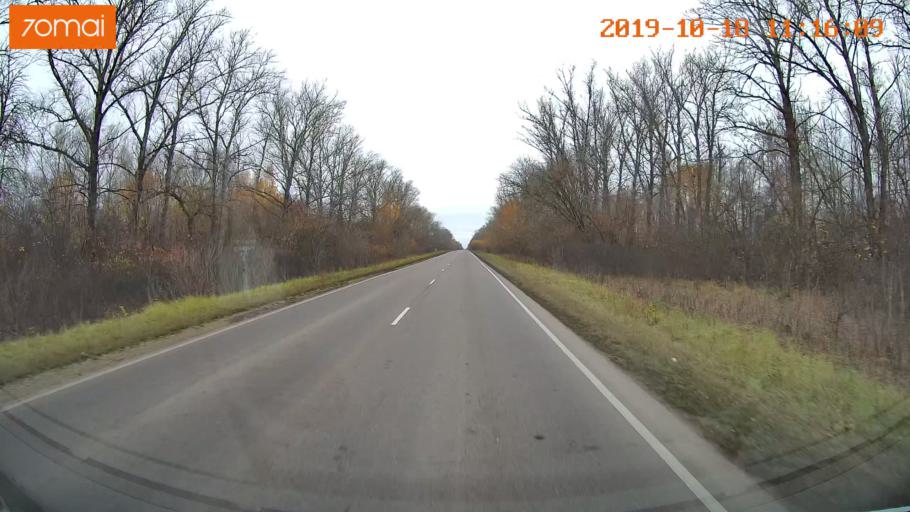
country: RU
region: Tula
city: Kimovsk
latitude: 54.0031
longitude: 38.5483
